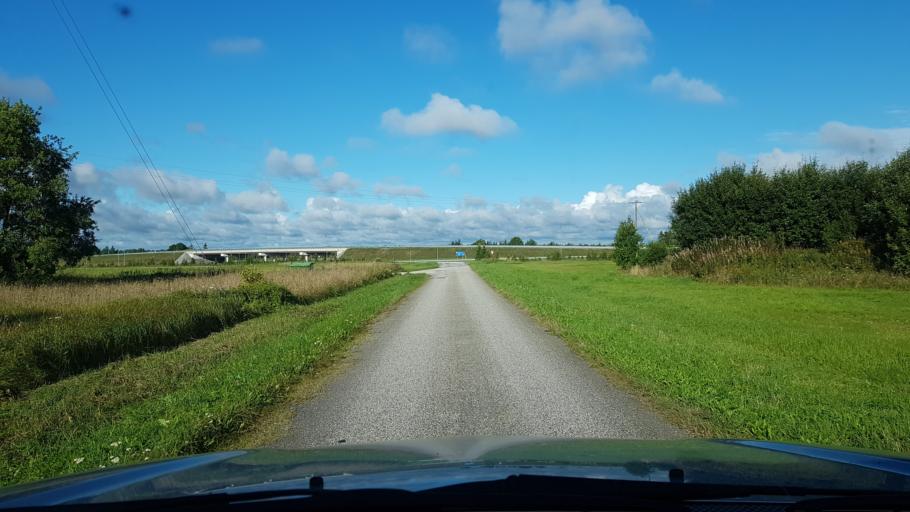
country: EE
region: Harju
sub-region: Rae vald
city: Vaida
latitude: 59.2518
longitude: 25.0203
